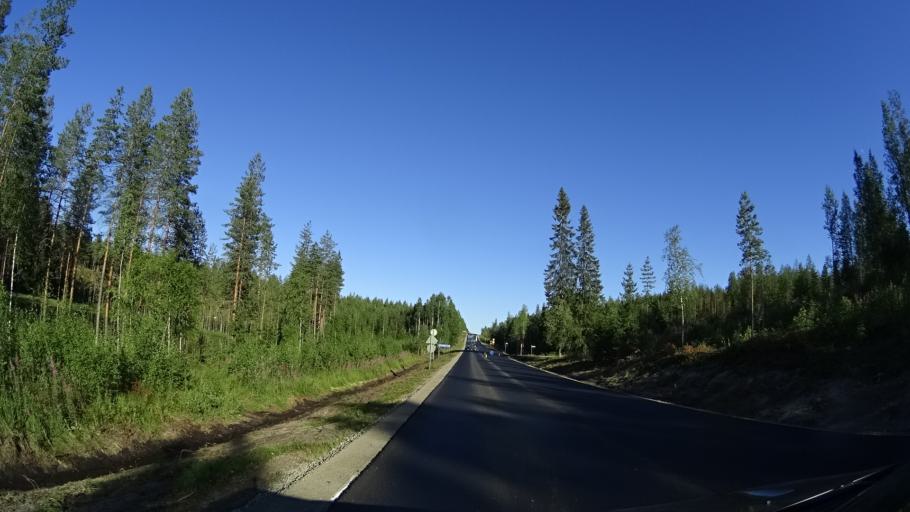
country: FI
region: North Karelia
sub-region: Pielisen Karjala
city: Valtimo
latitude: 63.5587
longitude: 28.6171
